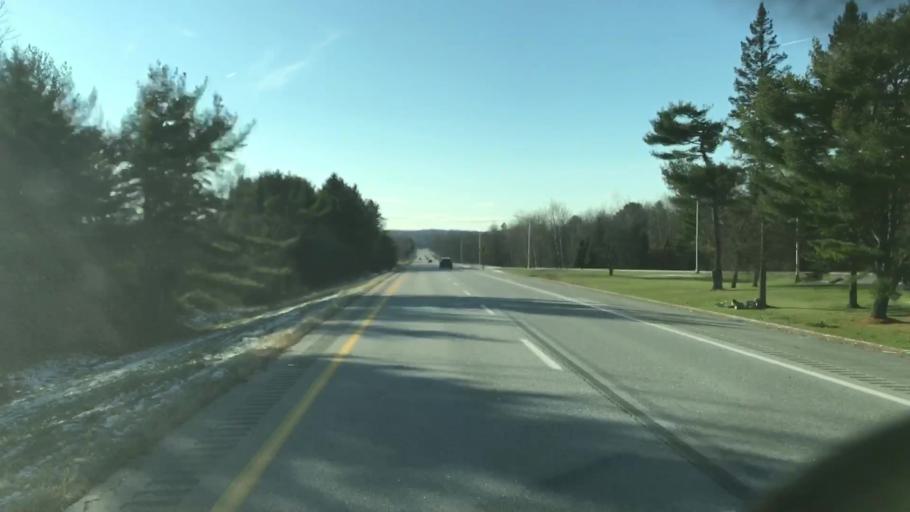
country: US
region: Maine
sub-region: Penobscot County
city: Hermon
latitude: 44.7668
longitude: -68.8860
